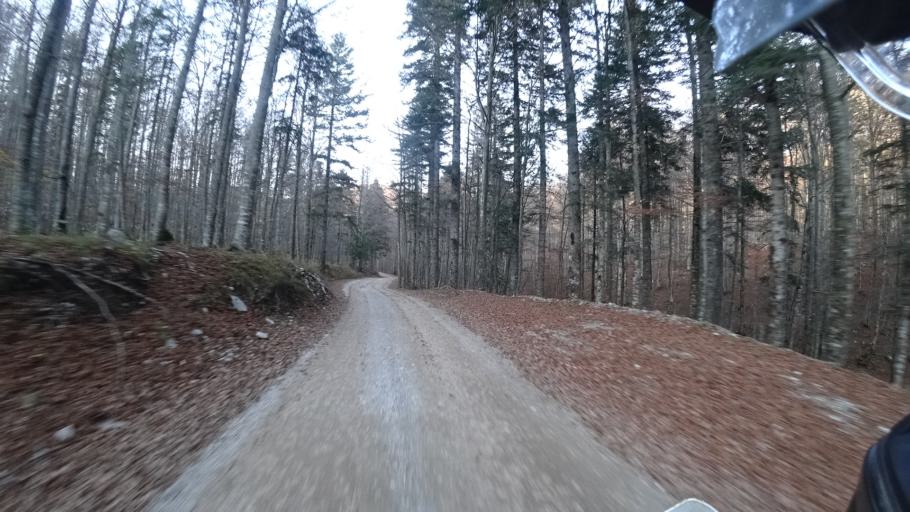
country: HR
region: Primorsko-Goranska
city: Klana
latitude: 45.4973
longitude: 14.4484
